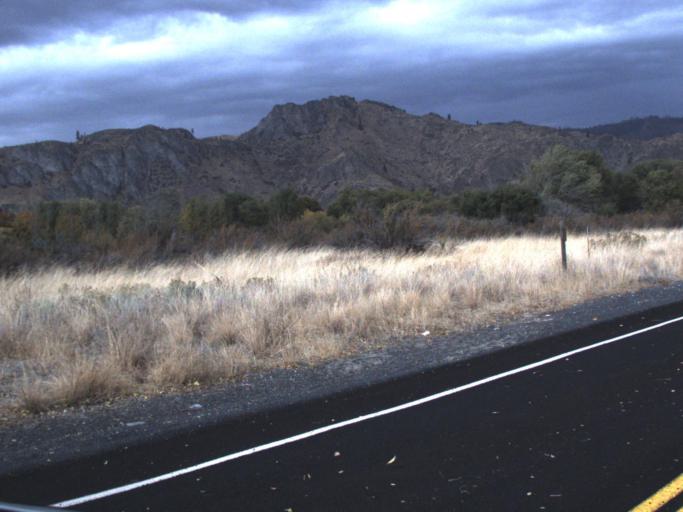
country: US
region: Washington
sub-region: Okanogan County
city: Coulee Dam
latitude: 47.9270
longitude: -118.6896
